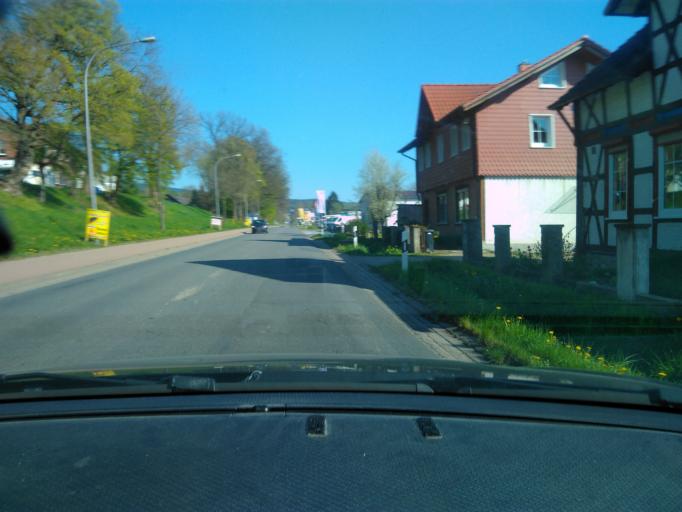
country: DE
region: Lower Saxony
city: Osterode am Harz
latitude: 51.7224
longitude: 10.2624
